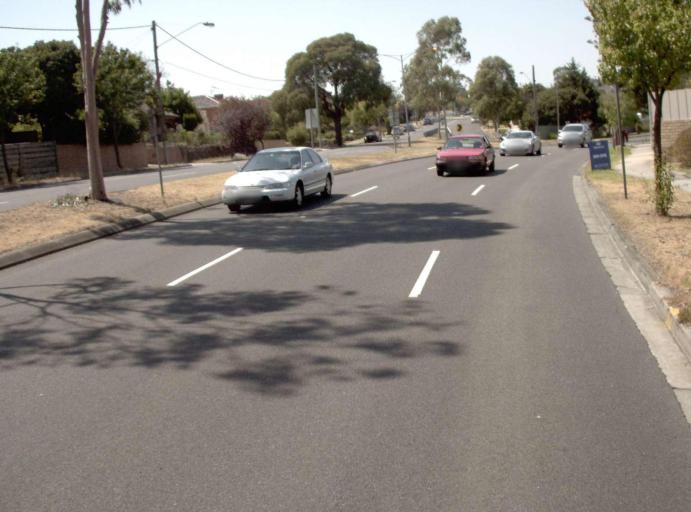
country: AU
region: Victoria
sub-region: Manningham
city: Bulleen
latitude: -37.7686
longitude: 145.0971
